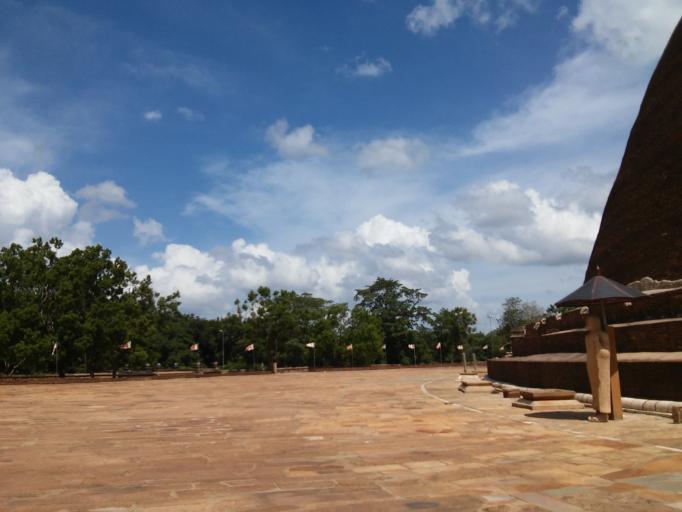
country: LK
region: North Central
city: Anuradhapura
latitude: 8.3715
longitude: 80.3955
